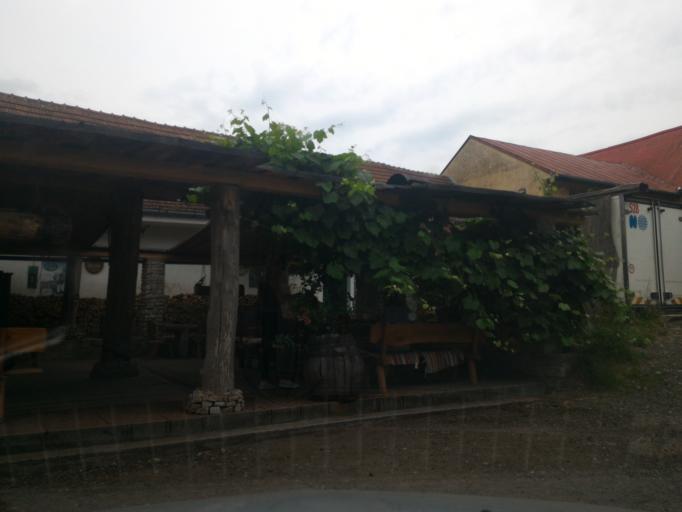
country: CZ
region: Vysocina
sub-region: Okres Jihlava
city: Telc
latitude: 49.1804
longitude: 15.4134
